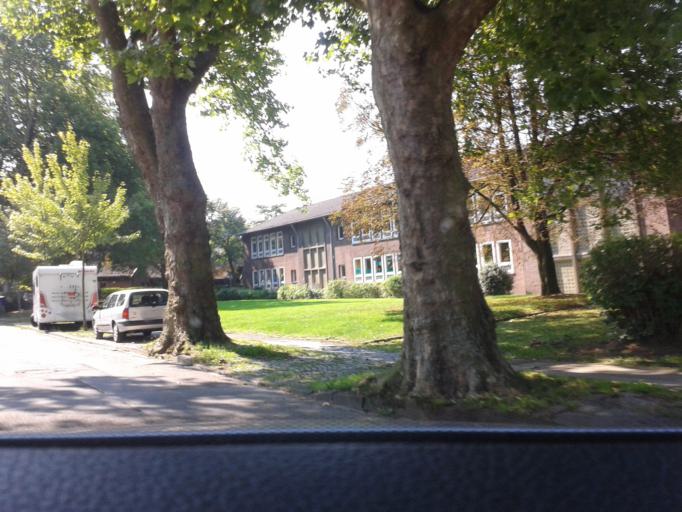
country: DE
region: North Rhine-Westphalia
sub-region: Regierungsbezirk Dusseldorf
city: Muelheim (Ruhr)
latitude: 51.4283
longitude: 6.8330
